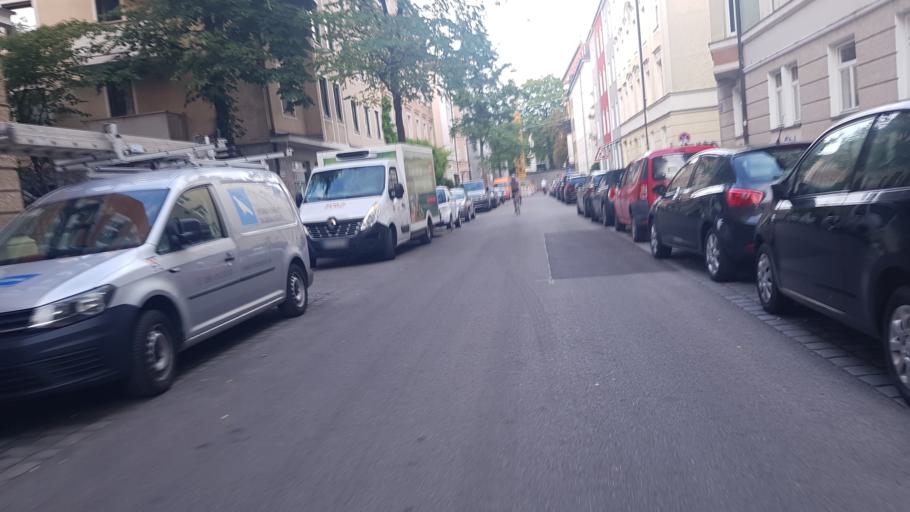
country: DE
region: Bavaria
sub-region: Upper Bavaria
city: Munich
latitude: 48.1311
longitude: 11.6000
